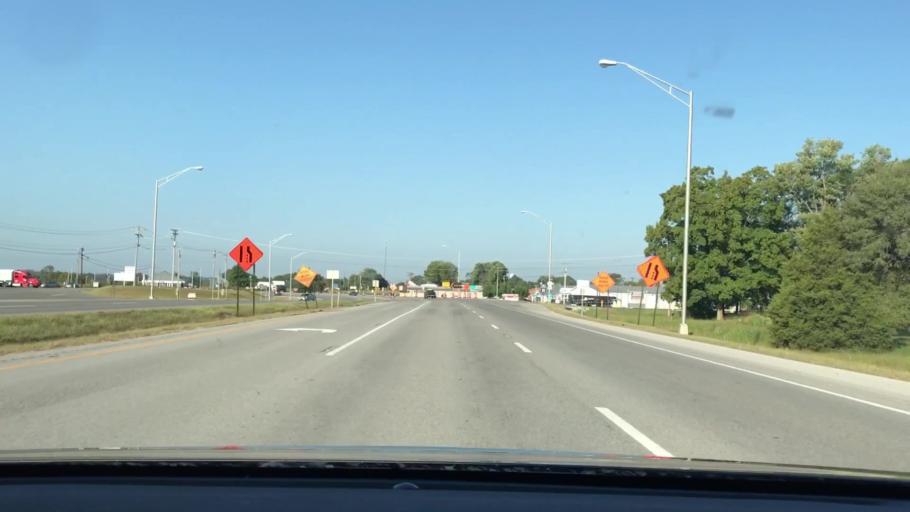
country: US
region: Kentucky
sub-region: Trigg County
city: Cadiz
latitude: 36.8678
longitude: -87.7910
